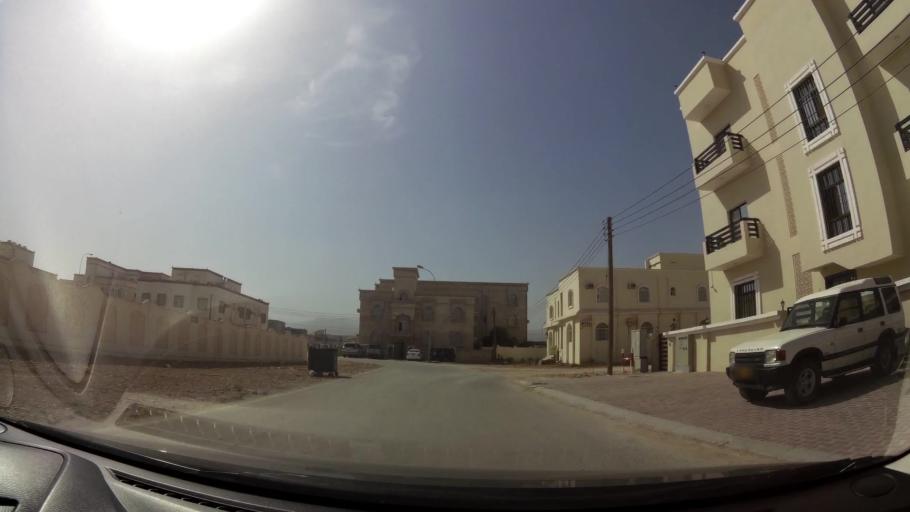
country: OM
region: Zufar
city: Salalah
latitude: 17.0039
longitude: 54.0151
